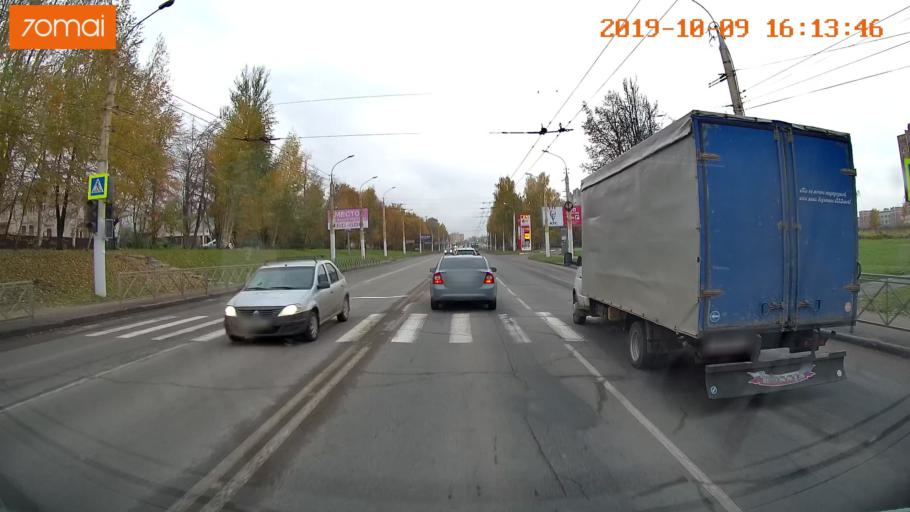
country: RU
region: Kostroma
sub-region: Kostromskoy Rayon
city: Kostroma
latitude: 57.7451
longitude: 40.9269
